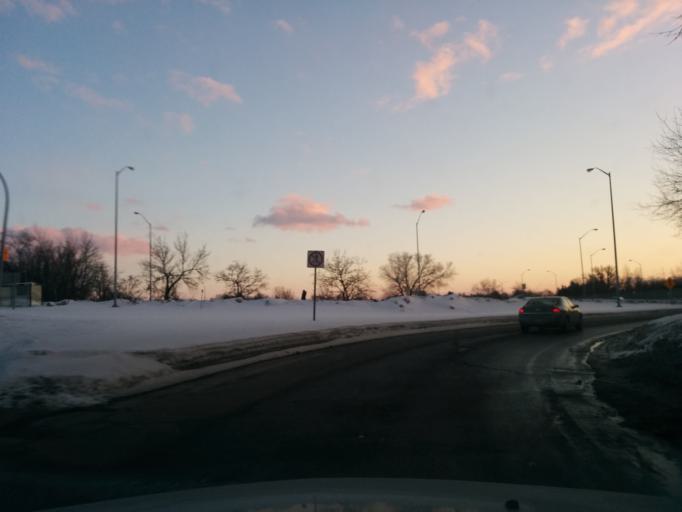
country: CA
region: Ontario
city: Bells Corners
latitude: 45.3627
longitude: -75.7693
